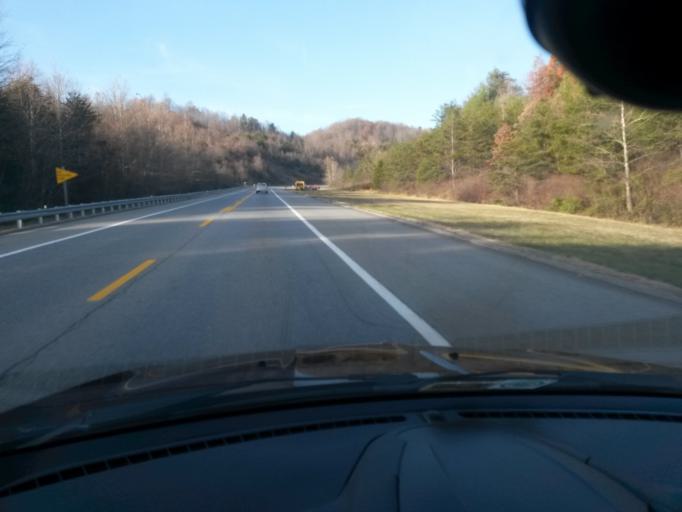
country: US
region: Virginia
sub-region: Alleghany County
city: Clifton Forge
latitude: 37.7567
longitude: -79.7878
